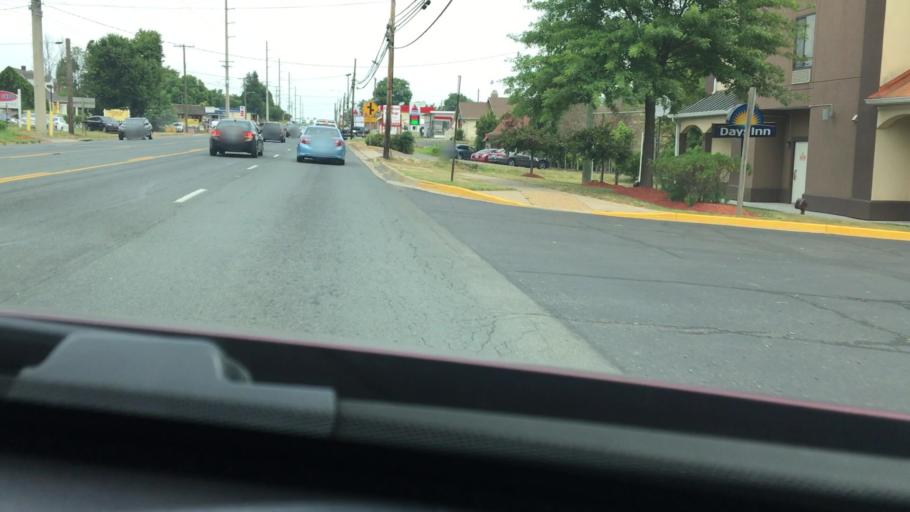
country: US
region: Virginia
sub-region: Prince William County
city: Yorkshire
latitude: 38.7882
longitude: -77.4487
